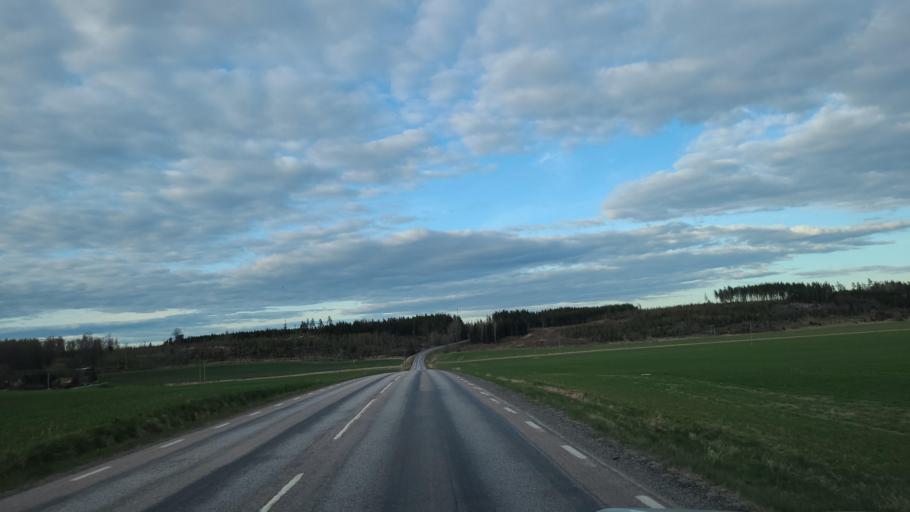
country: SE
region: Soedermanland
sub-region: Nykopings Kommun
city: Stigtomta
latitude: 58.7486
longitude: 16.7209
